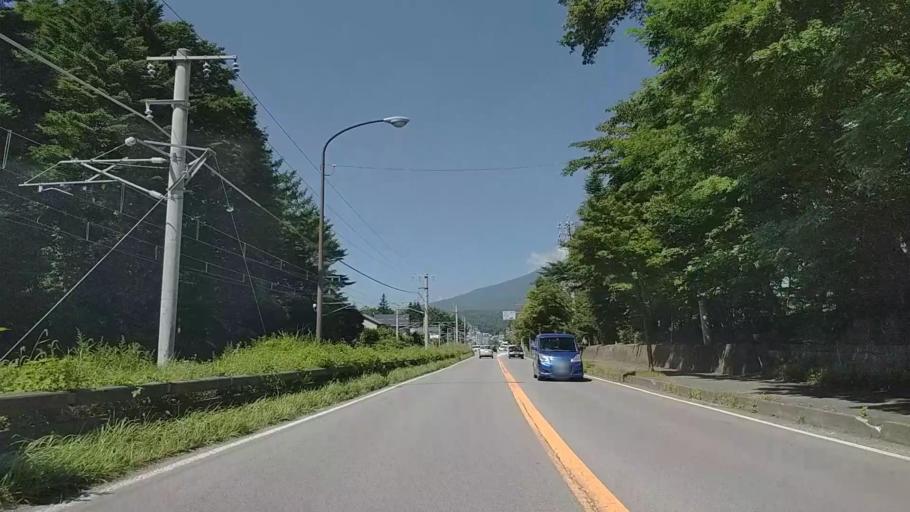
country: JP
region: Nagano
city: Komoro
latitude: 36.3442
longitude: 138.6049
